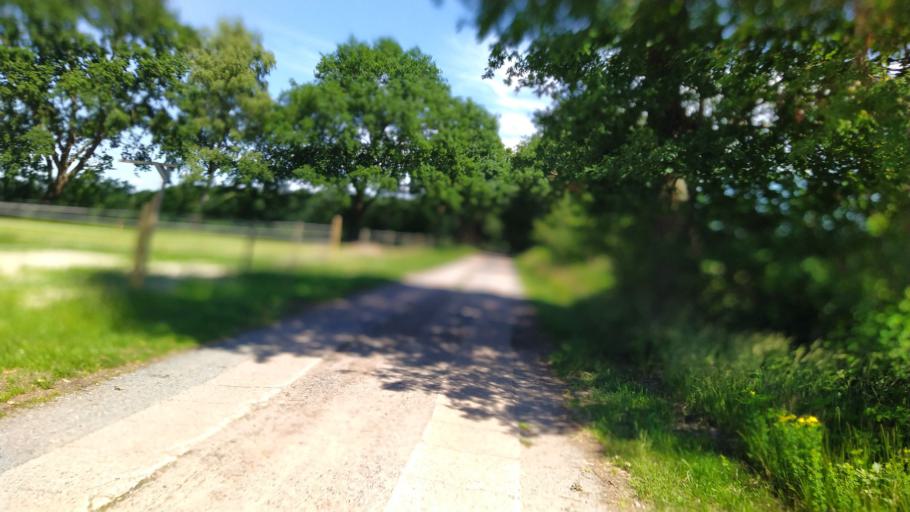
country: DE
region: Lower Saxony
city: Bargstedt
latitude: 53.4897
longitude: 9.4356
